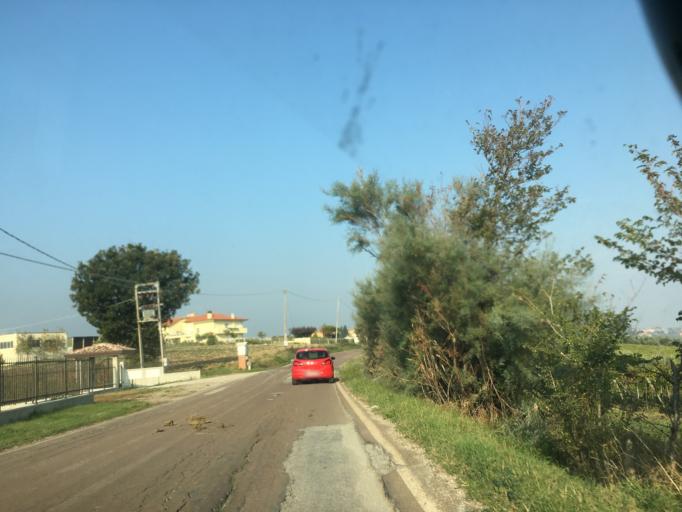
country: IT
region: Emilia-Romagna
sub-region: Provincia di Rimini
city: San Clemente
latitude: 43.9472
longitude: 12.6162
